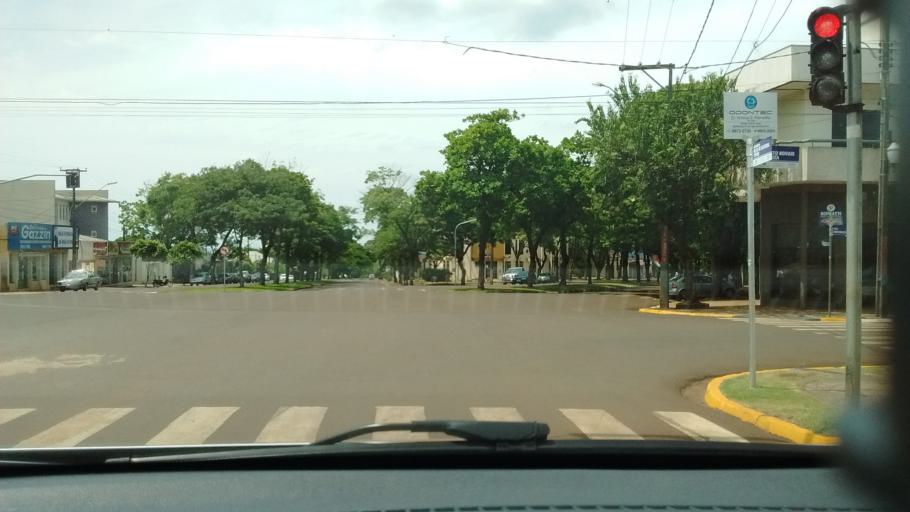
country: BR
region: Parana
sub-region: Corbelia
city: Corbelia
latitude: -24.5387
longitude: -52.9903
